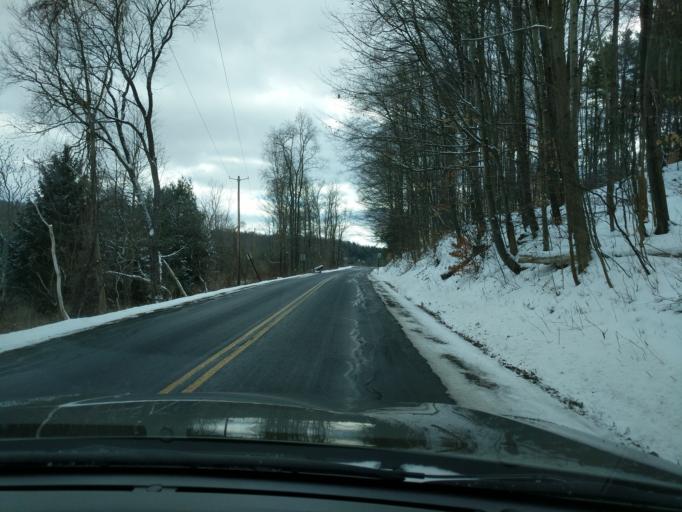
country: US
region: New York
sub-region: Tompkins County
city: Northeast Ithaca
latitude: 42.4148
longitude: -76.3813
